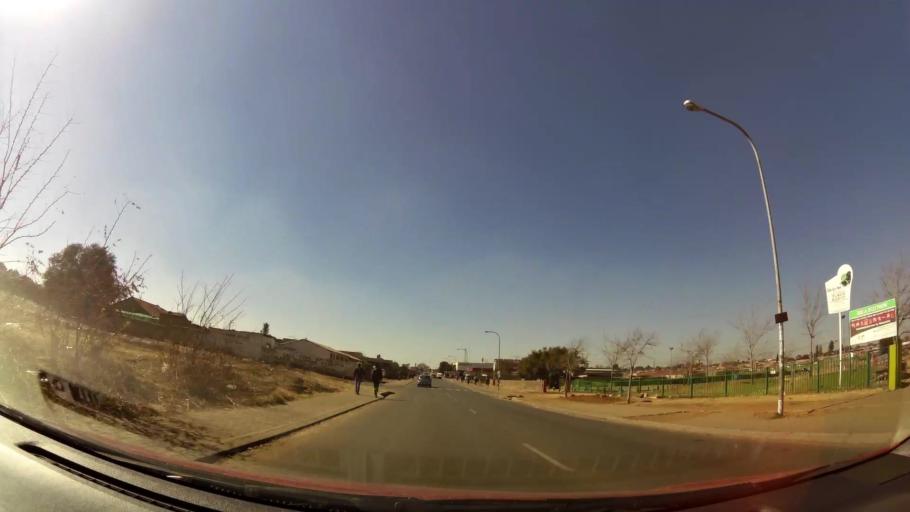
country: ZA
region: Gauteng
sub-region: City of Johannesburg Metropolitan Municipality
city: Soweto
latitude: -26.2405
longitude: 27.8445
